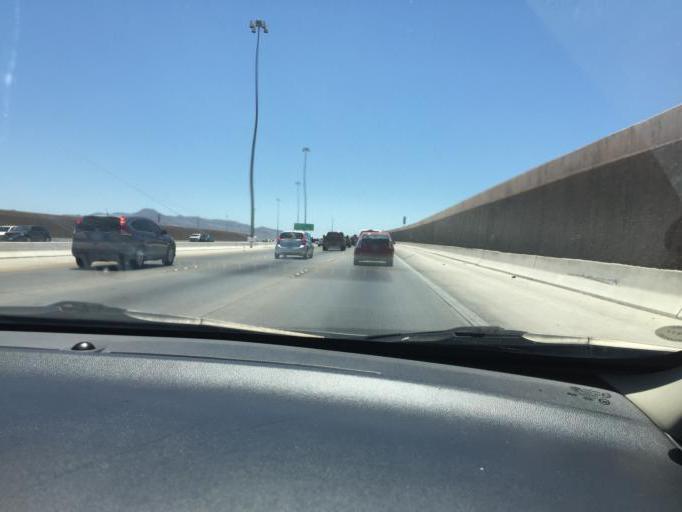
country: US
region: Nevada
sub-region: Clark County
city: Whitney
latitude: 36.0313
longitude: -115.1321
